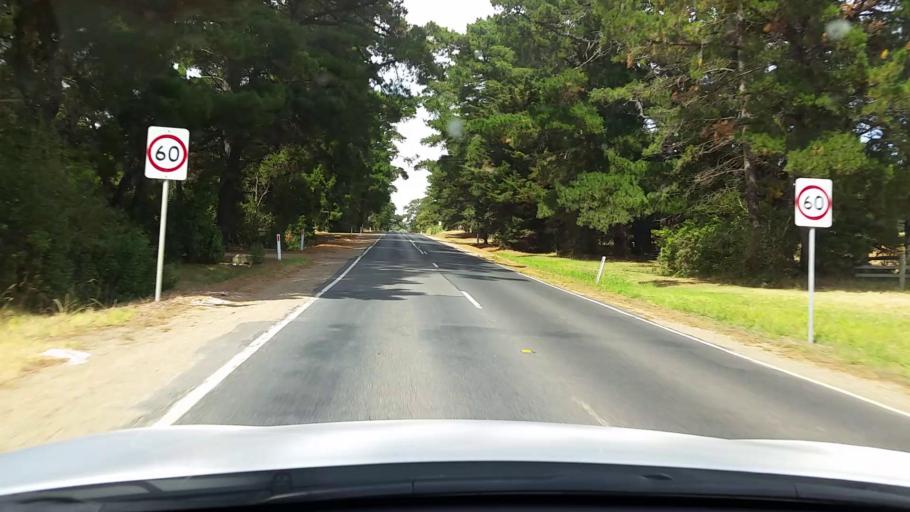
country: AU
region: Victoria
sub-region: Mornington Peninsula
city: Merricks
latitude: -38.4655
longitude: 145.0206
